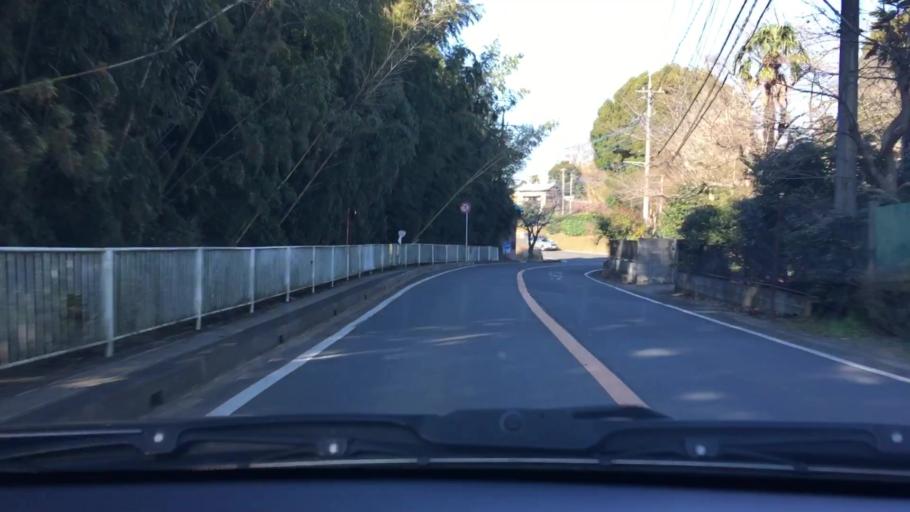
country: JP
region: Chiba
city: Shisui
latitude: 35.6991
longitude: 140.2534
